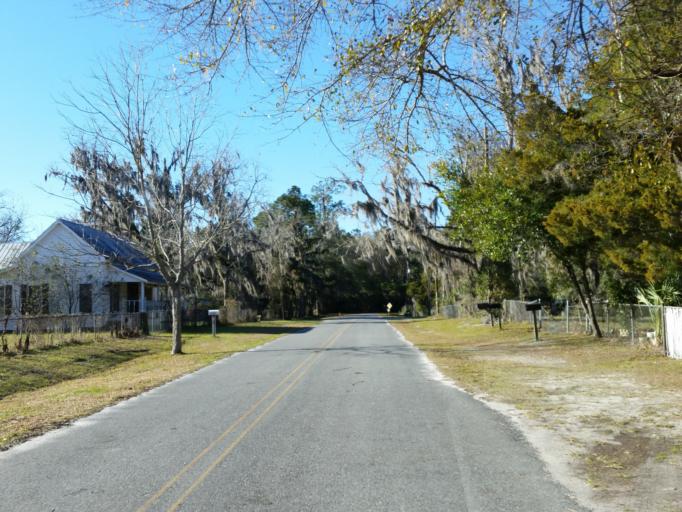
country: US
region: Georgia
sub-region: Echols County
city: Statenville
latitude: 30.6055
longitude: -83.0982
